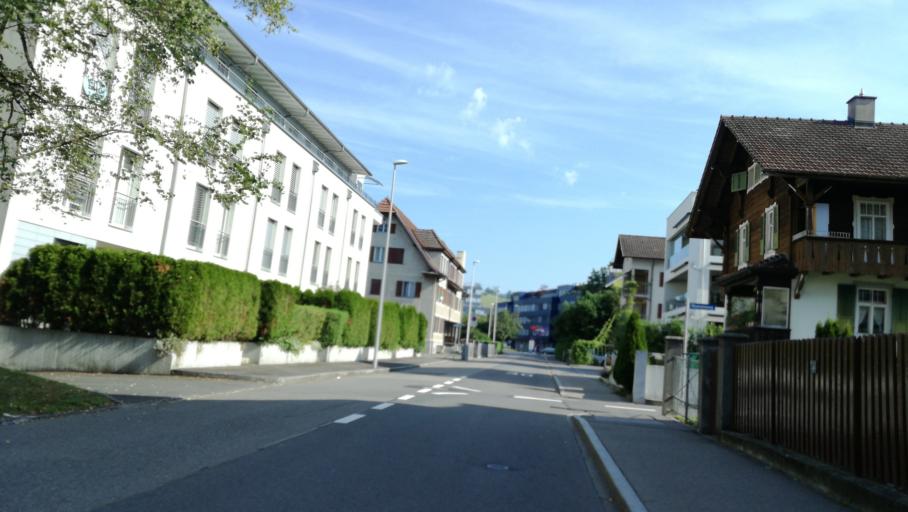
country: CH
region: Zug
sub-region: Zug
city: Baar
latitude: 47.1983
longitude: 8.5251
